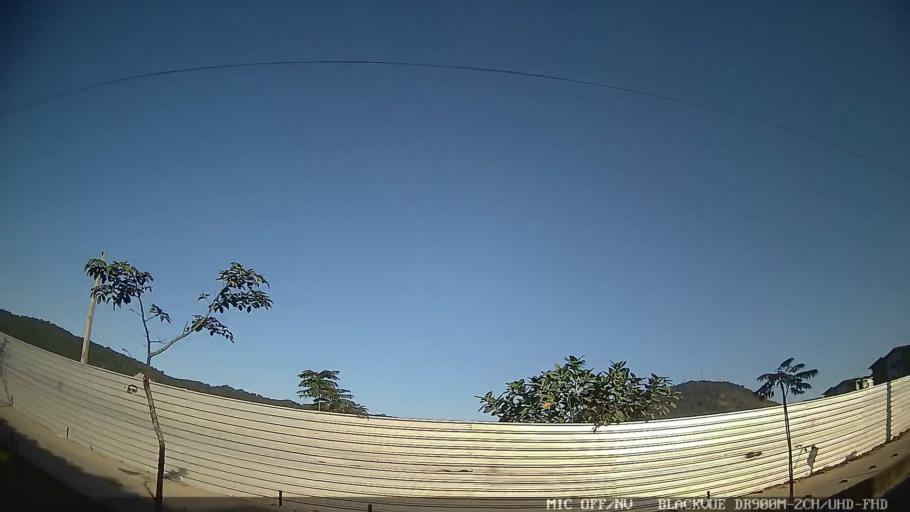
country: BR
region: Sao Paulo
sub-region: Guaruja
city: Guaruja
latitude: -23.9656
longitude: -46.2526
